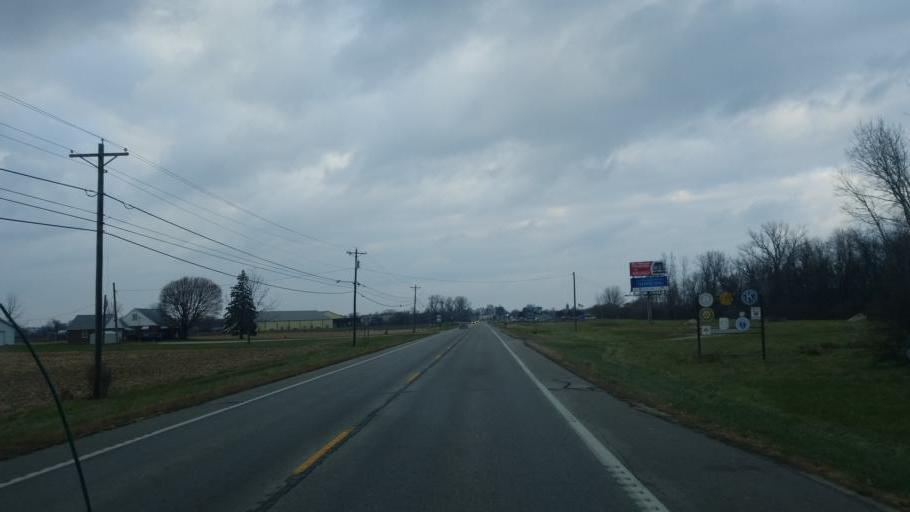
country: US
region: Ohio
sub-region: Mercer County
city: Celina
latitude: 40.5284
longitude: -84.5772
